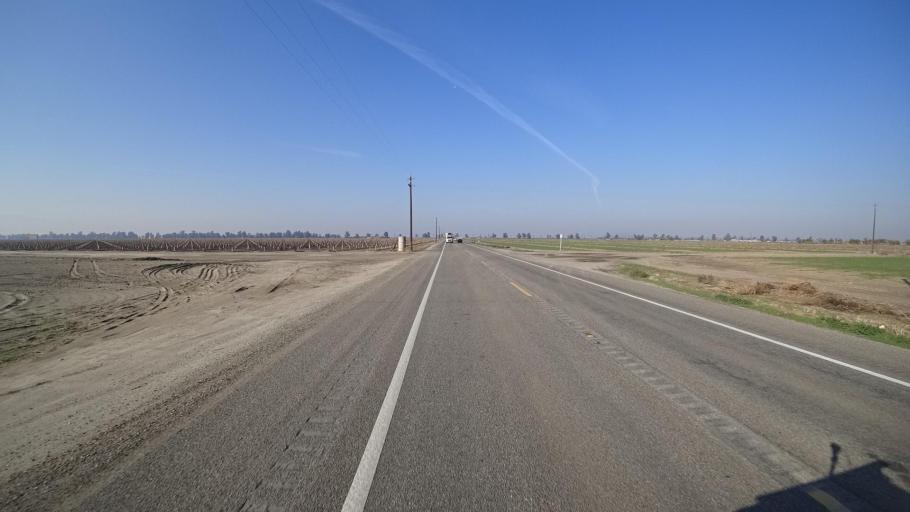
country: US
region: California
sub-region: Kern County
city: Greenfield
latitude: 35.2085
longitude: -118.9847
